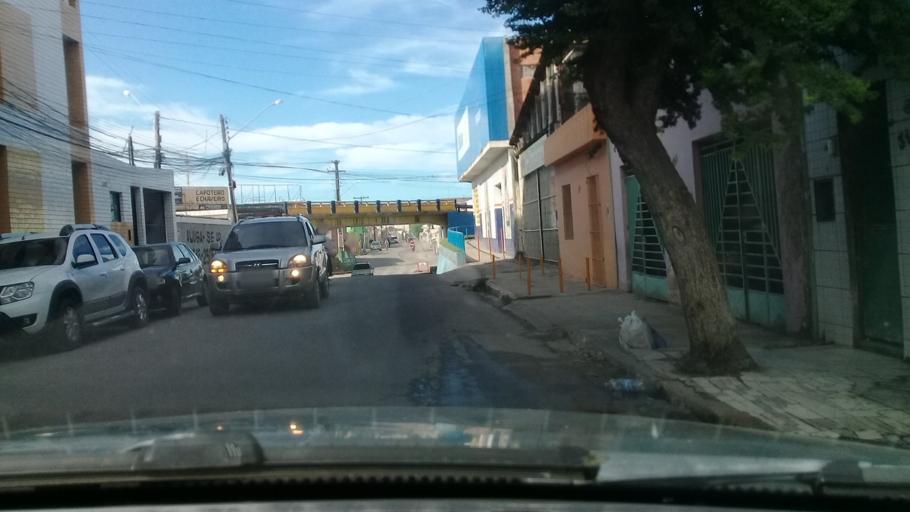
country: BR
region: Pernambuco
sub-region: Vitoria De Santo Antao
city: Vitoria de Santo Antao
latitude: -8.1126
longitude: -35.2904
